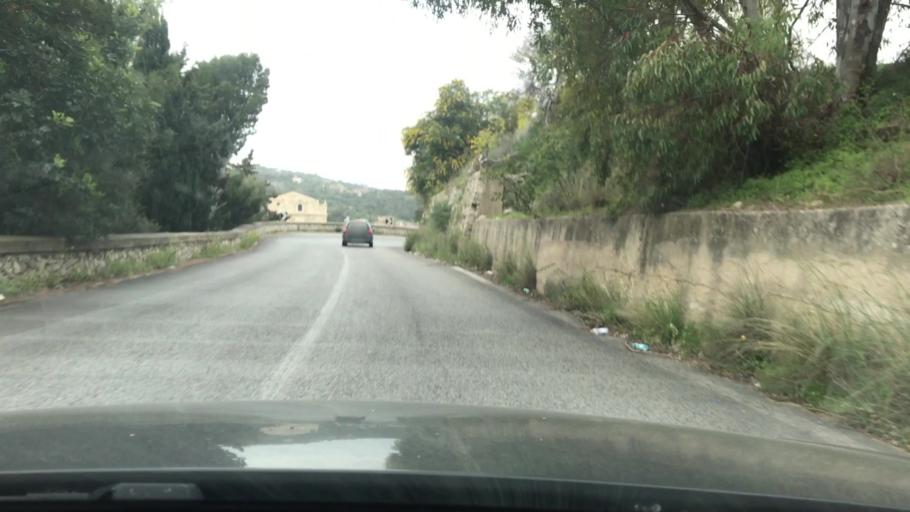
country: IT
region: Sicily
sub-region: Ragusa
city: Scicli
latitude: 36.7958
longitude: 14.7111
